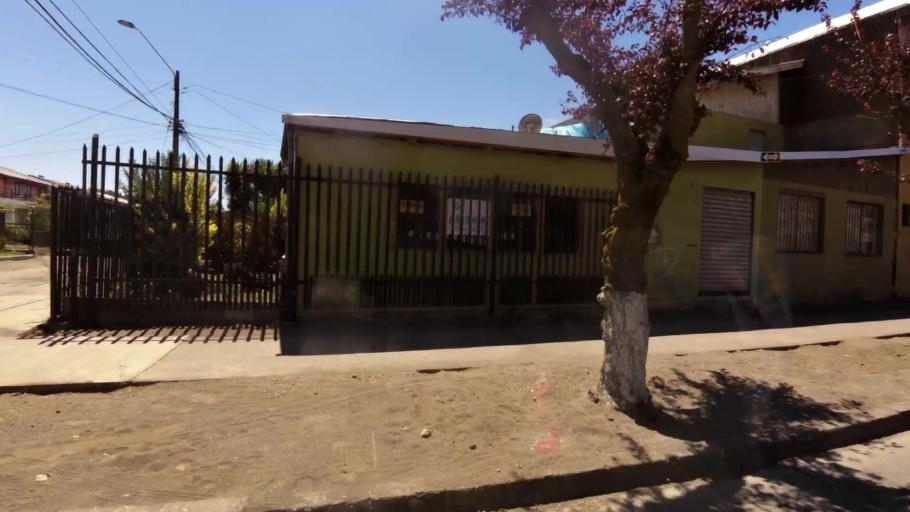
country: CL
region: Biobio
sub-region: Provincia de Concepcion
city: Talcahuano
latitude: -36.7612
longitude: -73.0915
